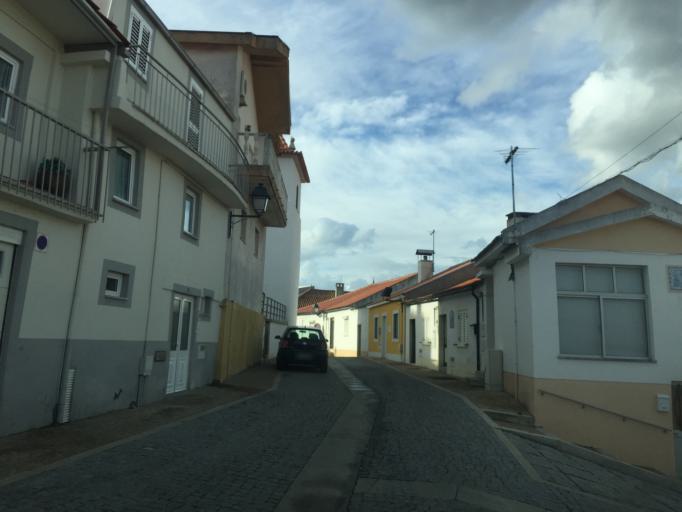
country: PT
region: Braganca
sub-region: Alfandega da Fe
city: Alfandega da Fe
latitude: 41.3416
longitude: -6.9654
